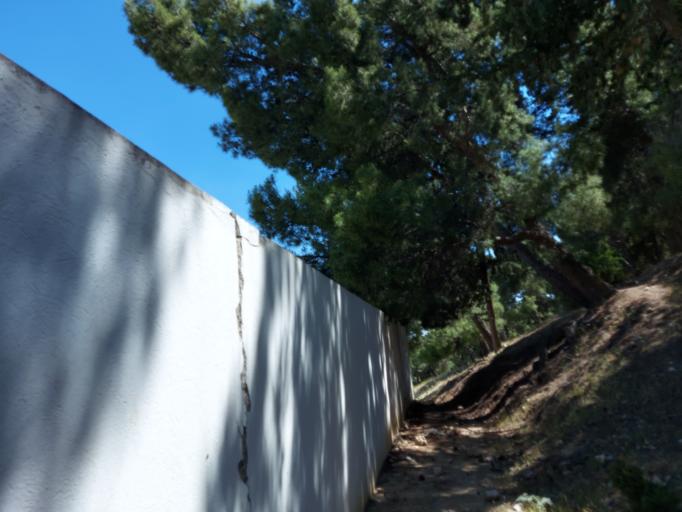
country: TN
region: Kef
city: El Kef
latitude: 36.1839
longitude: 8.7252
